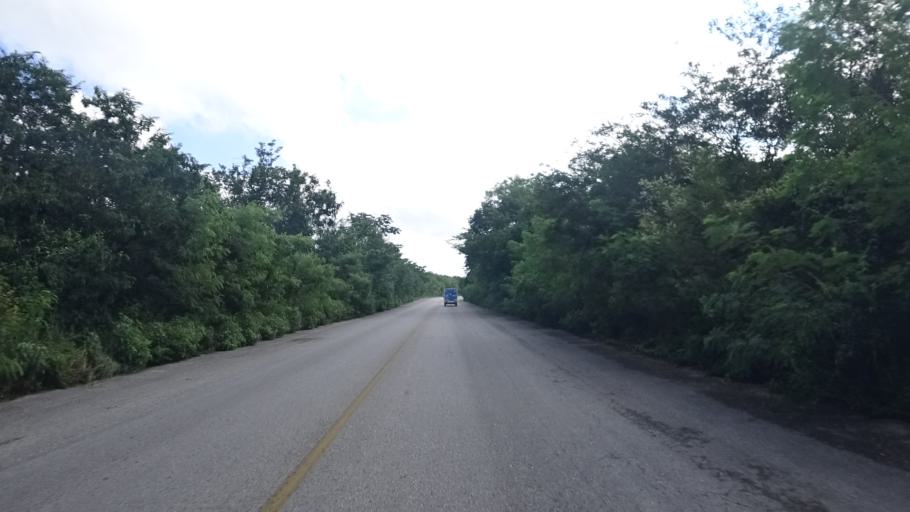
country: MX
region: Yucatan
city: Valladolid
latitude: 20.7232
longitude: -88.2182
